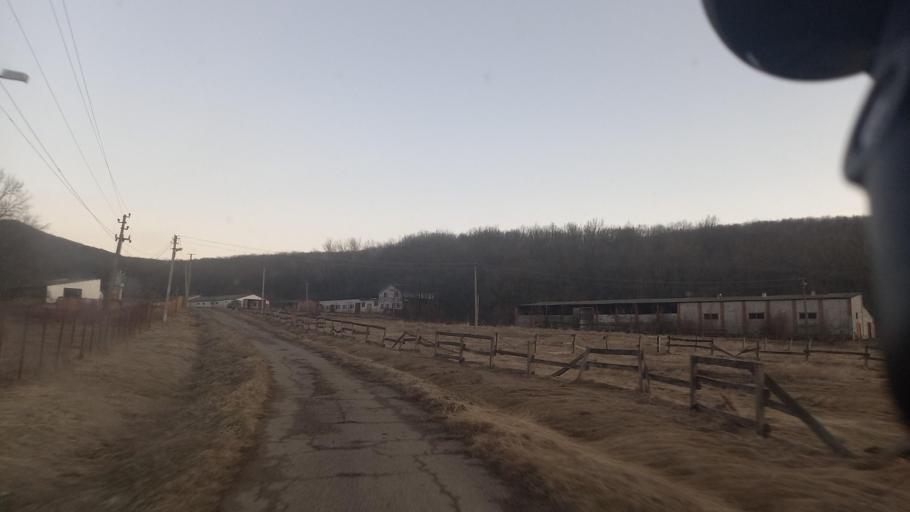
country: RU
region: Krasnodarskiy
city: Smolenskaya
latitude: 44.7252
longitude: 38.8426
